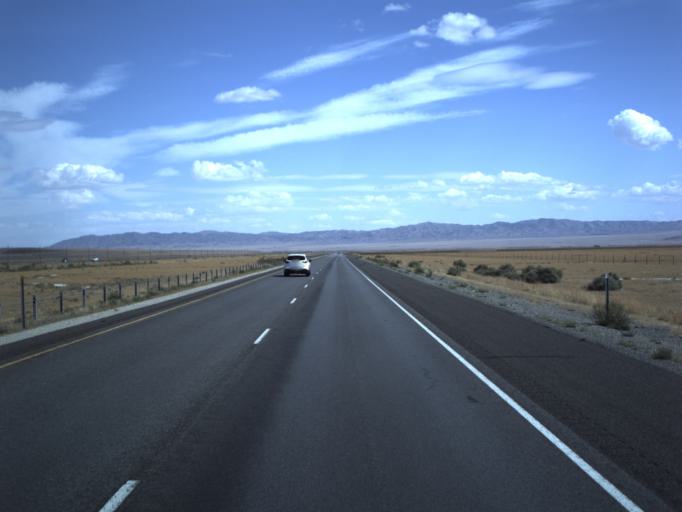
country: US
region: Utah
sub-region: Tooele County
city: Grantsville
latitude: 40.7257
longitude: -113.1990
